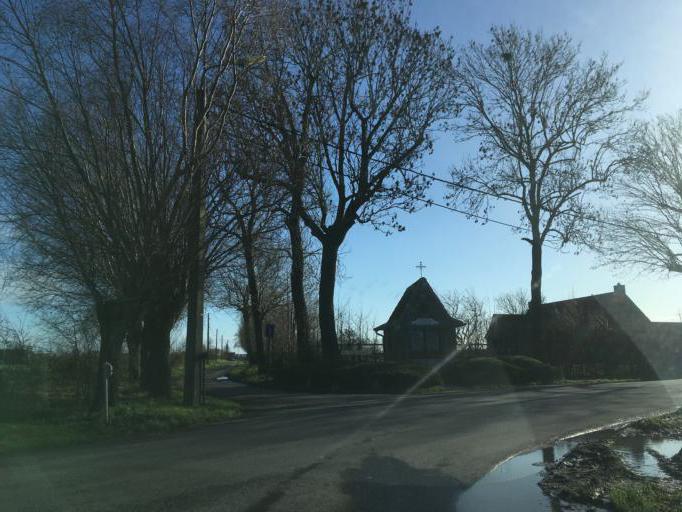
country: BE
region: Flanders
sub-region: Provincie West-Vlaanderen
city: Ardooie
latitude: 50.9681
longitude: 3.1718
